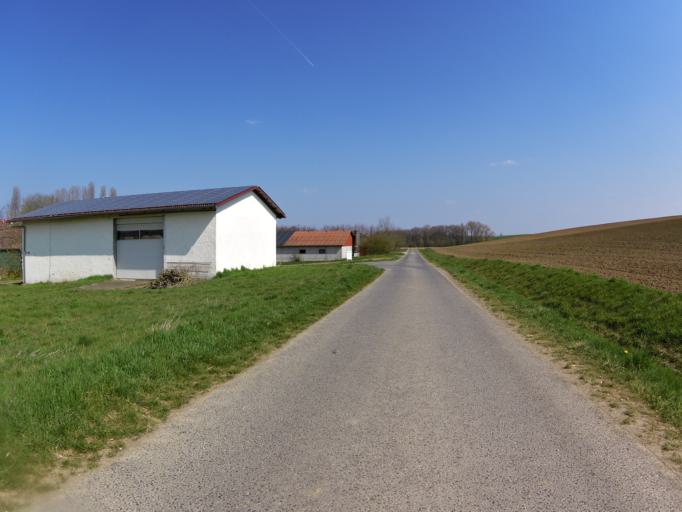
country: DE
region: Bavaria
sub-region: Regierungsbezirk Unterfranken
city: Dettelbach
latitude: 49.8213
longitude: 10.1264
